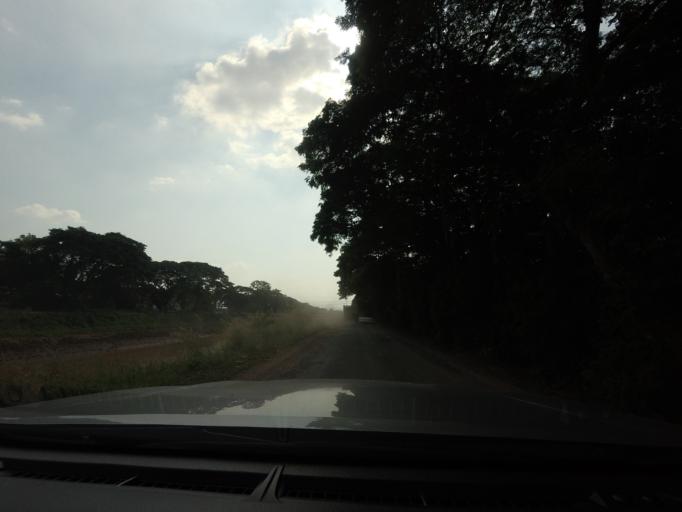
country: TH
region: Phitsanulok
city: Phitsanulok
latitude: 16.8037
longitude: 100.2129
